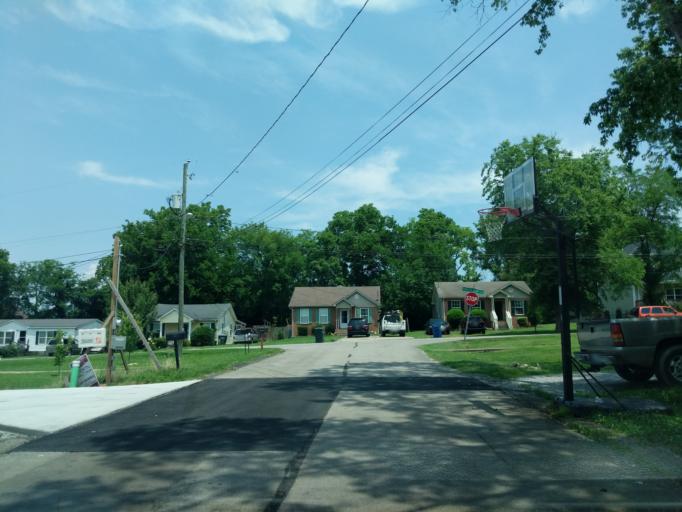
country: US
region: Tennessee
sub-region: Davidson County
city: Lakewood
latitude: 36.2291
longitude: -86.6335
